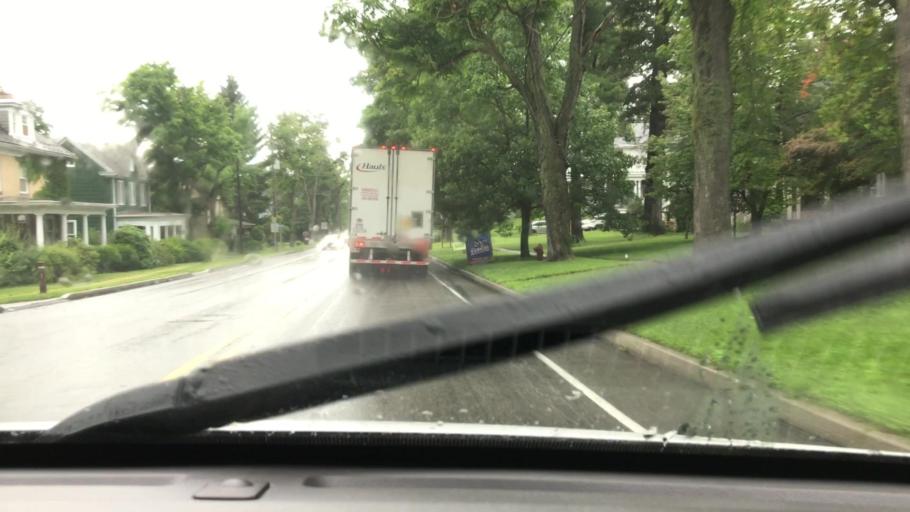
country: US
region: Pennsylvania
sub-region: Centre County
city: Philipsburg
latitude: 40.8944
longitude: -78.2186
